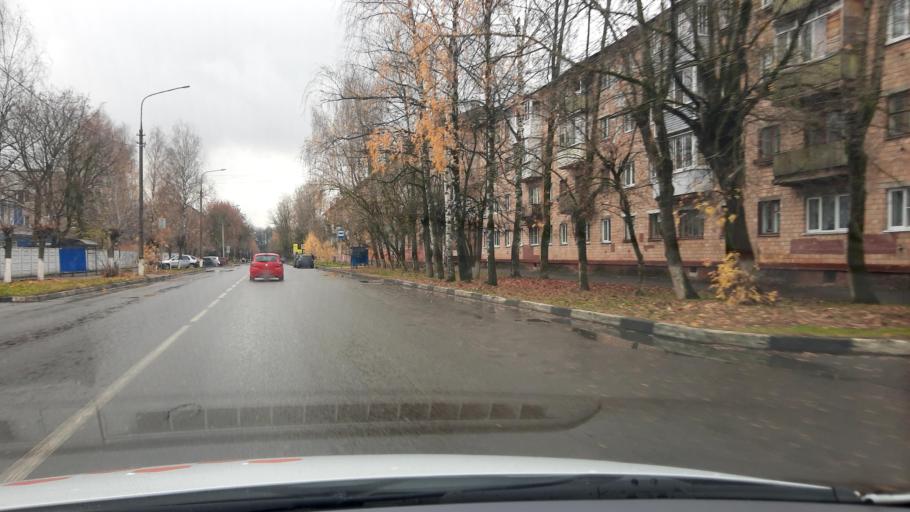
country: RU
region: Moskovskaya
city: Elektrostal'
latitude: 55.7902
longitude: 38.4470
